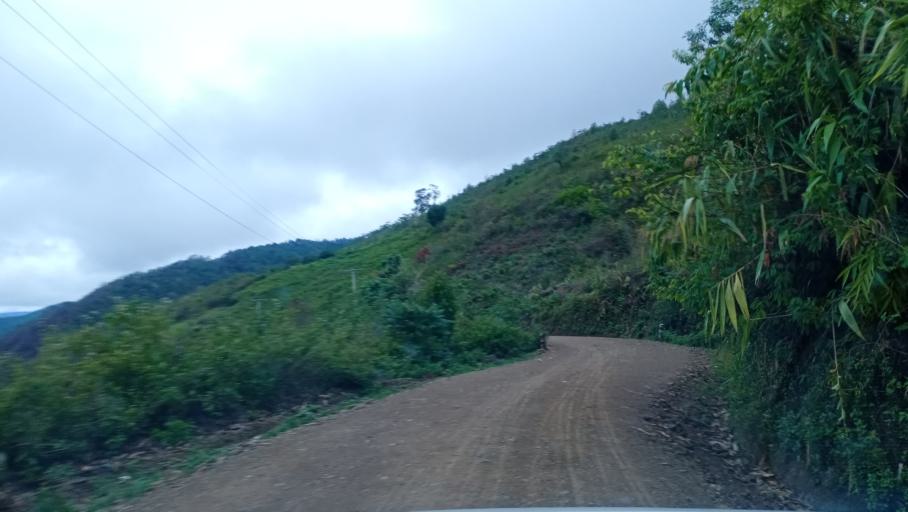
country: LA
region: Phongsali
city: Phongsali
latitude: 21.4559
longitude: 102.1604
